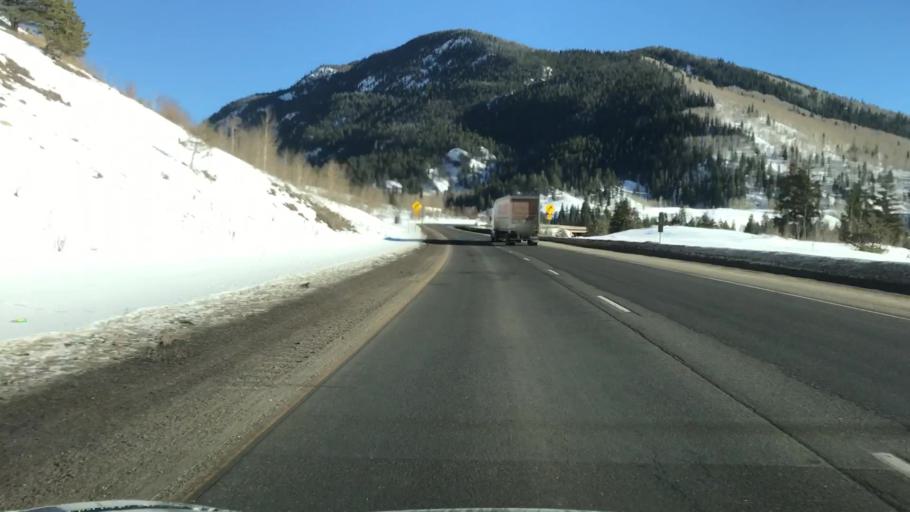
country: US
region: Colorado
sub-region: Eagle County
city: Vail
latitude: 39.6298
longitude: -106.2839
